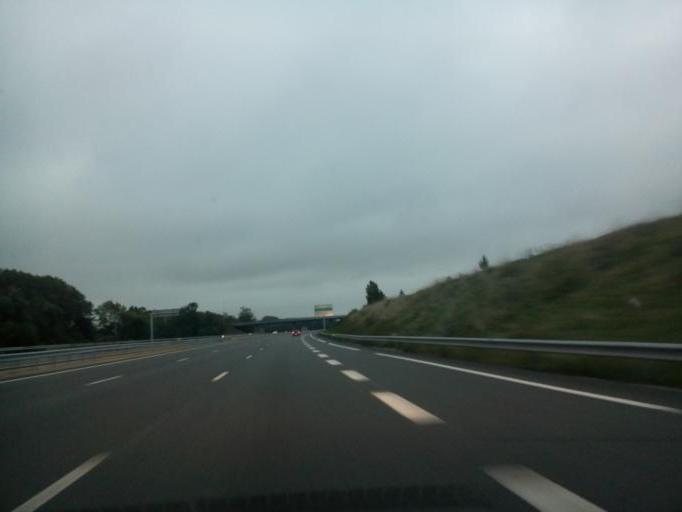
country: FR
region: Rhone-Alpes
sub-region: Departement de l'Isere
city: Saint-Alban-de-Roche
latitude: 45.6118
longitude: 5.2171
